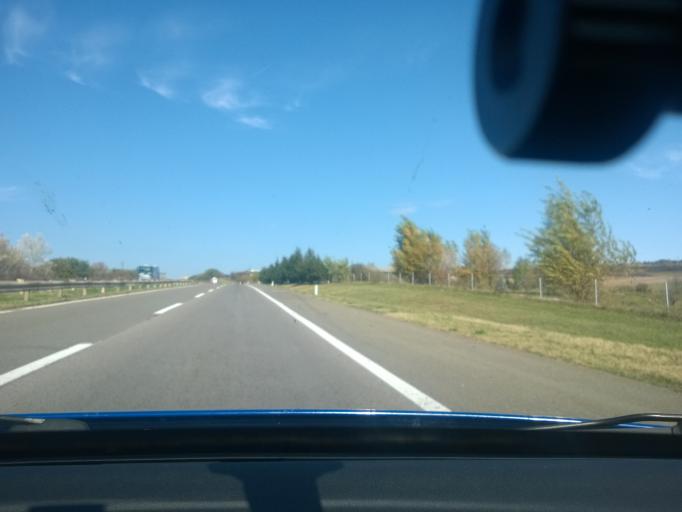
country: RS
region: Central Serbia
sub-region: Nisavski Okrug
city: Razanj
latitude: 43.6625
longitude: 21.5500
